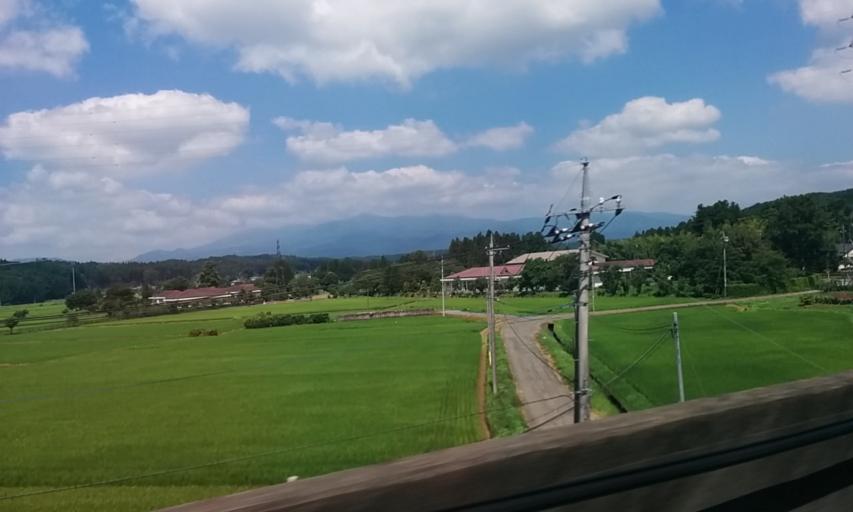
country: JP
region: Tochigi
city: Yaita
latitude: 36.8203
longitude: 139.9593
